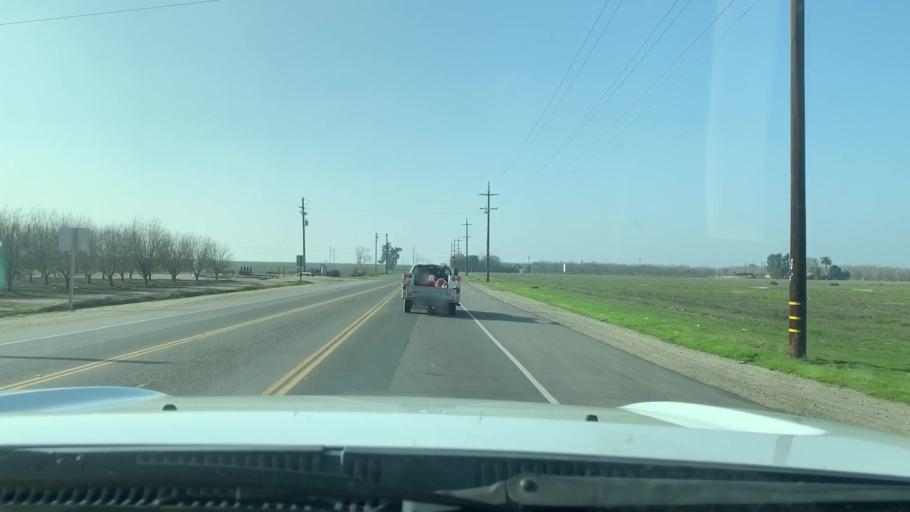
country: US
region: California
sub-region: Kern County
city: Wasco
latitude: 35.6016
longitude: -119.3614
